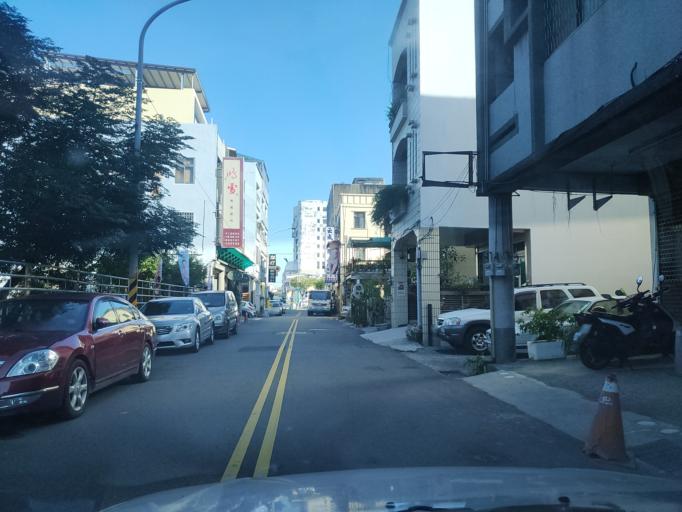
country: TW
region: Taiwan
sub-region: Miaoli
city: Miaoli
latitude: 24.5627
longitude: 120.8174
